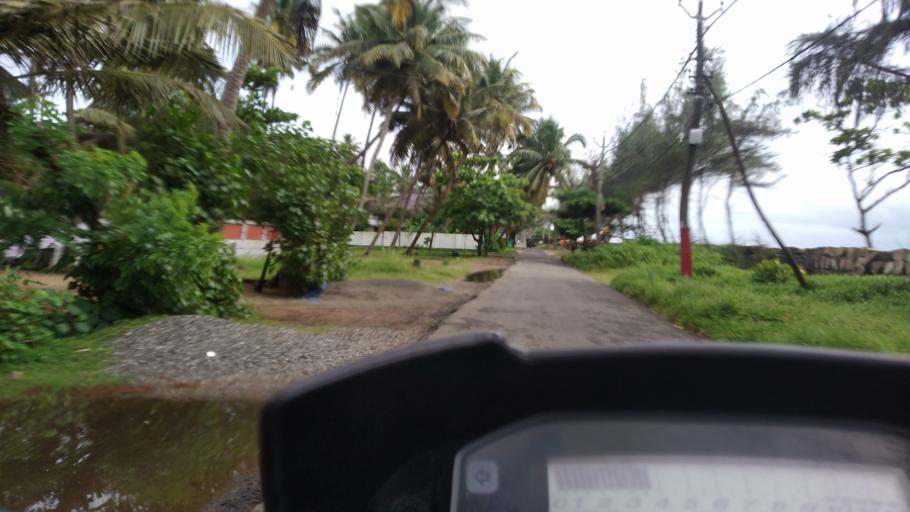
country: IN
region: Kerala
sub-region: Thrissur District
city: Kodungallur
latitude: 10.1574
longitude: 76.1730
